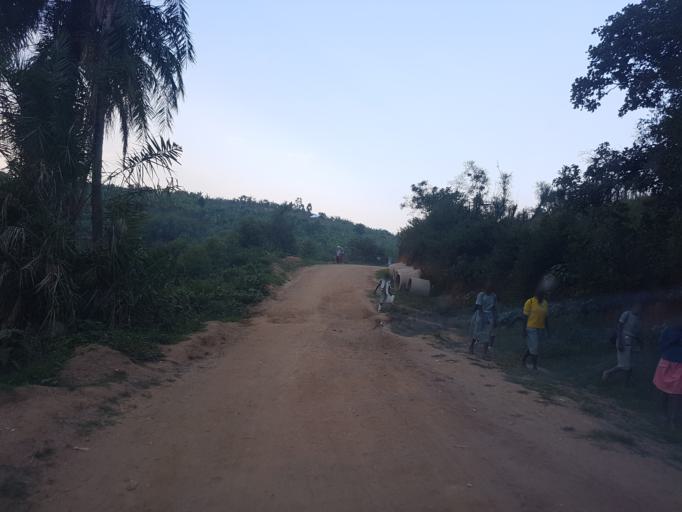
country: UG
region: Western Region
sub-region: Mitoma District
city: Mitoma
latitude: -0.6785
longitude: 29.9361
